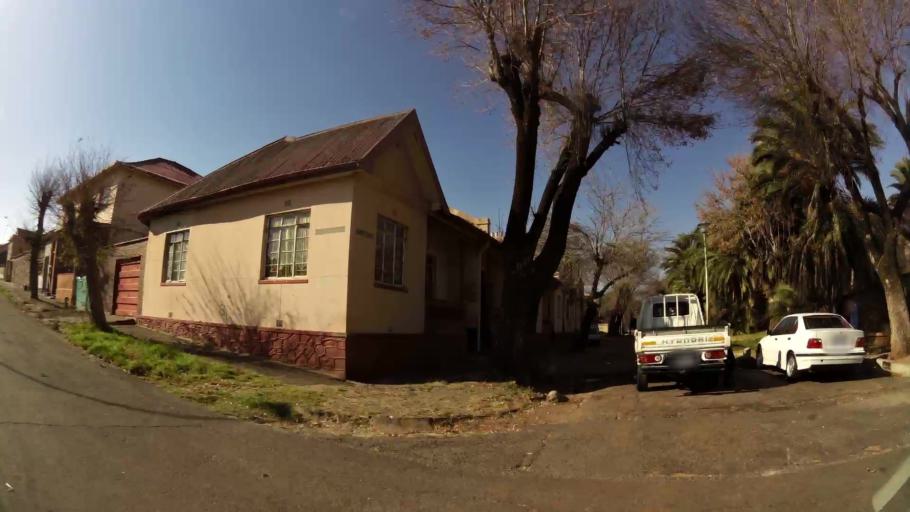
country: ZA
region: Gauteng
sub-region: City of Johannesburg Metropolitan Municipality
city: Johannesburg
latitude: -26.2056
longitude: 28.0714
